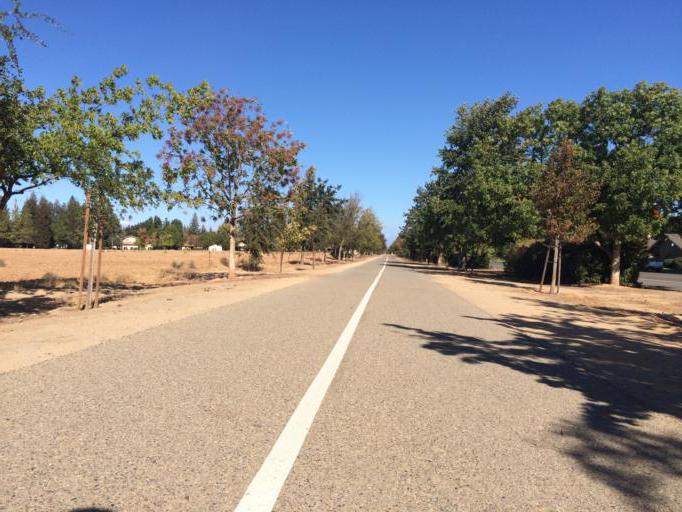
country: US
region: California
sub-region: Fresno County
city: Clovis
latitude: 36.8569
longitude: -119.7806
